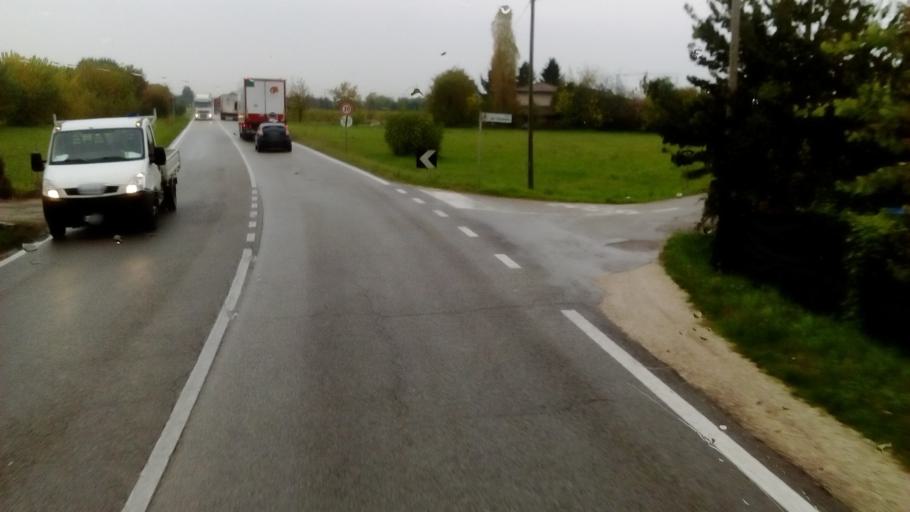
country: IT
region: Veneto
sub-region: Provincia di Vicenza
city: Breganze
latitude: 45.6885
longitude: 11.5626
